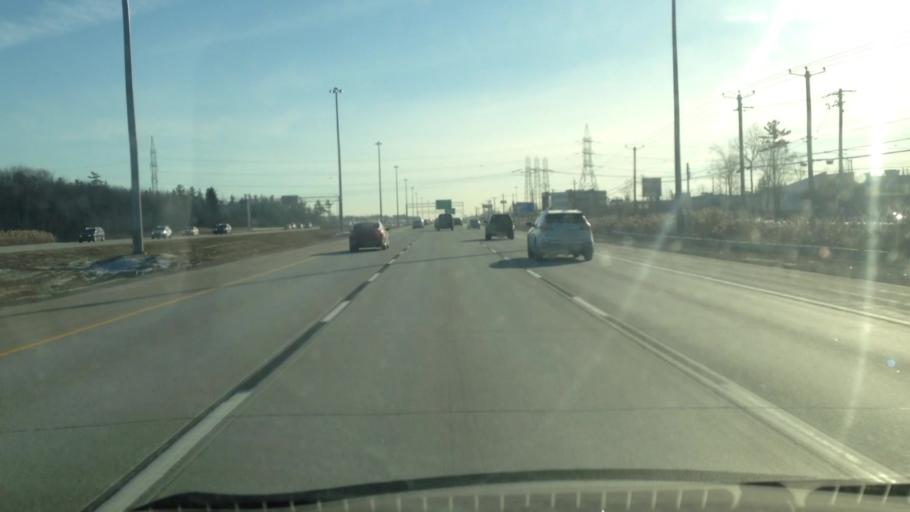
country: CA
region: Quebec
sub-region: Laurentides
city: Blainville
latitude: 45.6850
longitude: -73.9261
